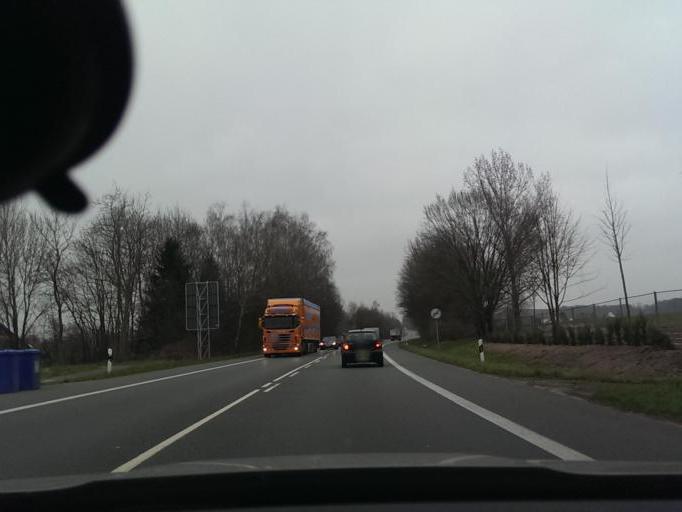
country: DE
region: North Rhine-Westphalia
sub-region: Regierungsbezirk Detmold
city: Delbruck
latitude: 51.7758
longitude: 8.5251
